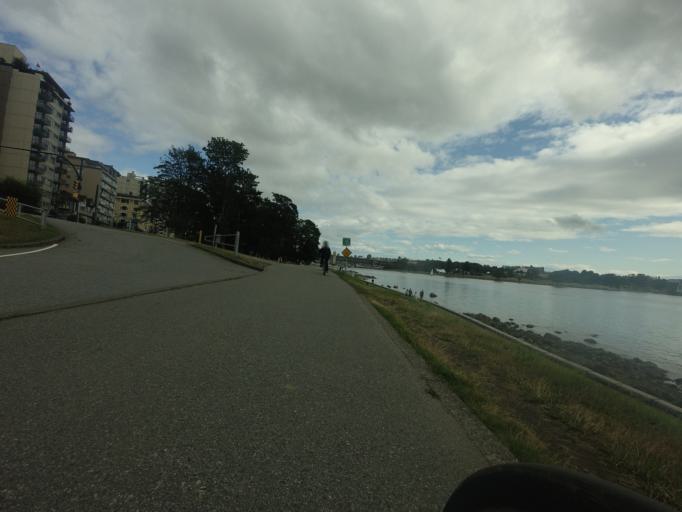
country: CA
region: British Columbia
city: West End
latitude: 49.2830
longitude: -123.1423
